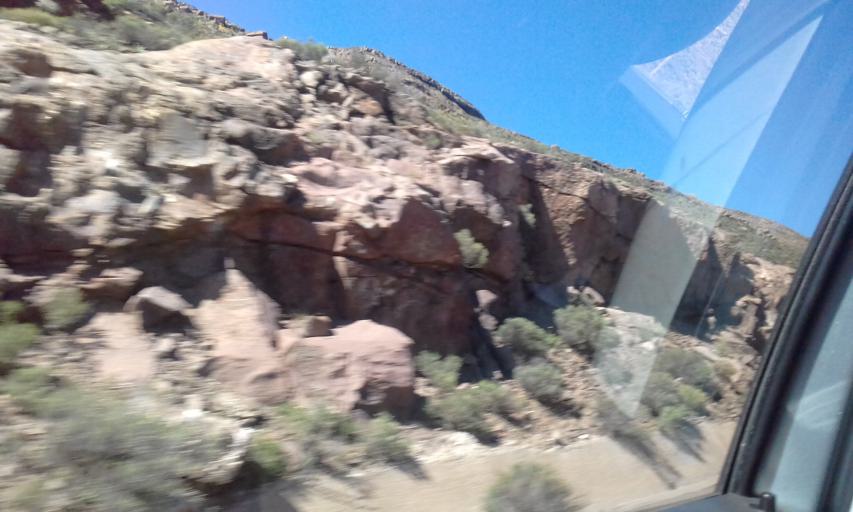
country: LS
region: Thaba-Tseka
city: Thaba-Tseka
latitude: -29.5085
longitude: 28.5008
